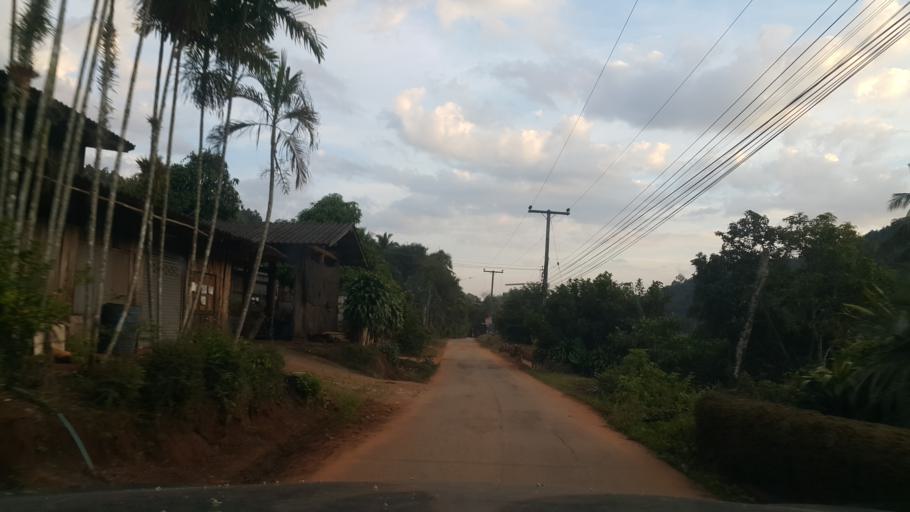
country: TH
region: Chiang Mai
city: Samoeng
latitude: 18.9791
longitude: 98.6771
